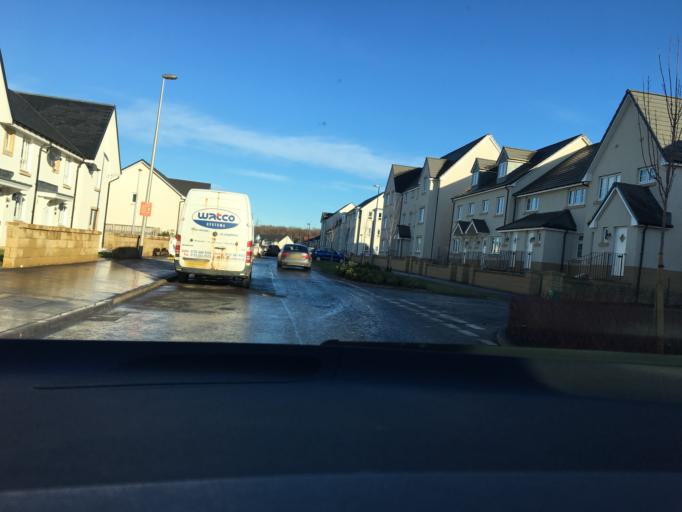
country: GB
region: Scotland
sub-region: Midlothian
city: Dalkeith
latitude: 55.8963
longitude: -3.0413
